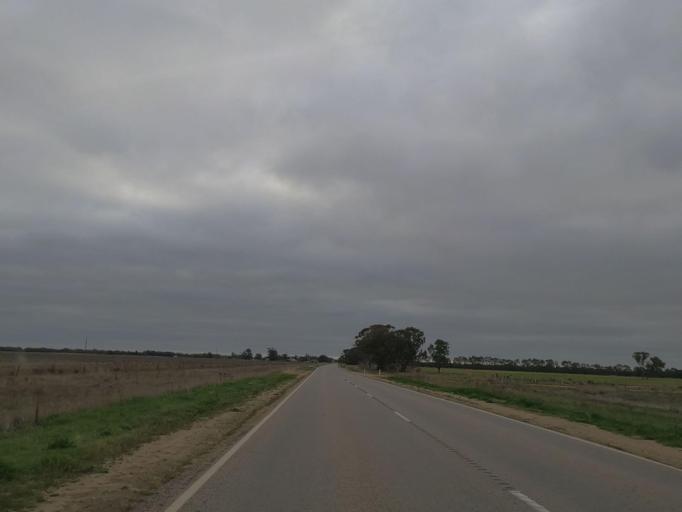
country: AU
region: Victoria
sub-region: Greater Bendigo
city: Long Gully
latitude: -36.1476
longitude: 143.9324
